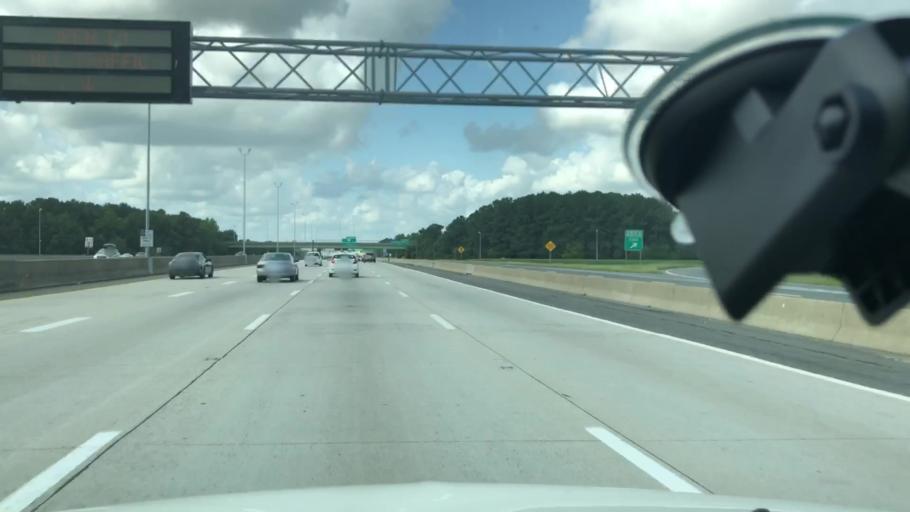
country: US
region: Virginia
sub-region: City of Chesapeake
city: Chesapeake
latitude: 36.7866
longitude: -76.2294
